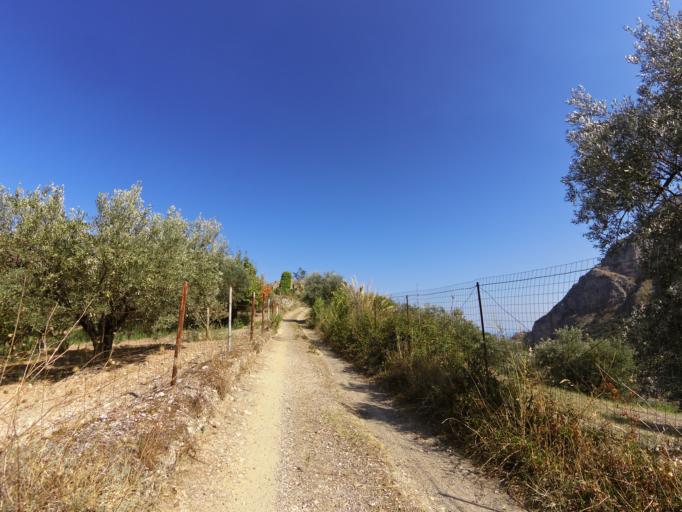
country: IT
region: Calabria
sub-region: Provincia di Reggio Calabria
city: Bivongi
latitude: 38.4914
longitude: 16.4621
